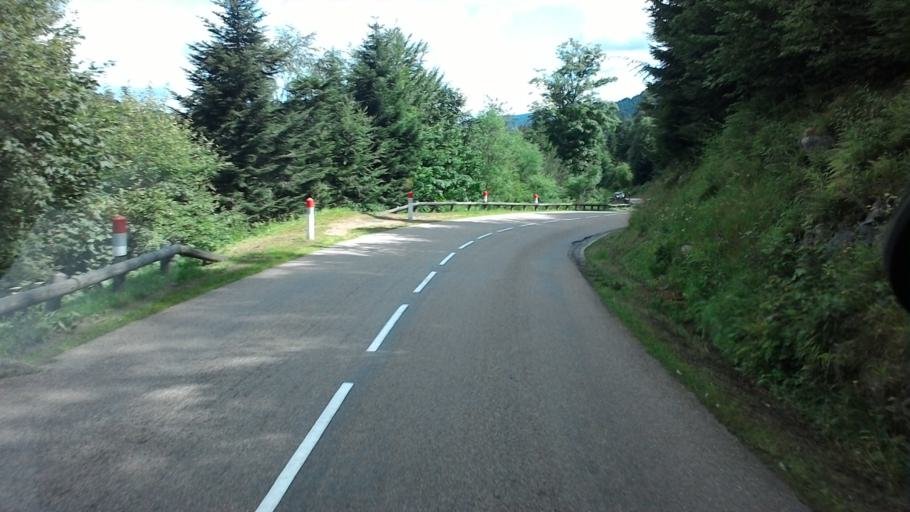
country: FR
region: Lorraine
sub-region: Departement des Vosges
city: Gerardmer
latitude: 48.0383
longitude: 6.8632
